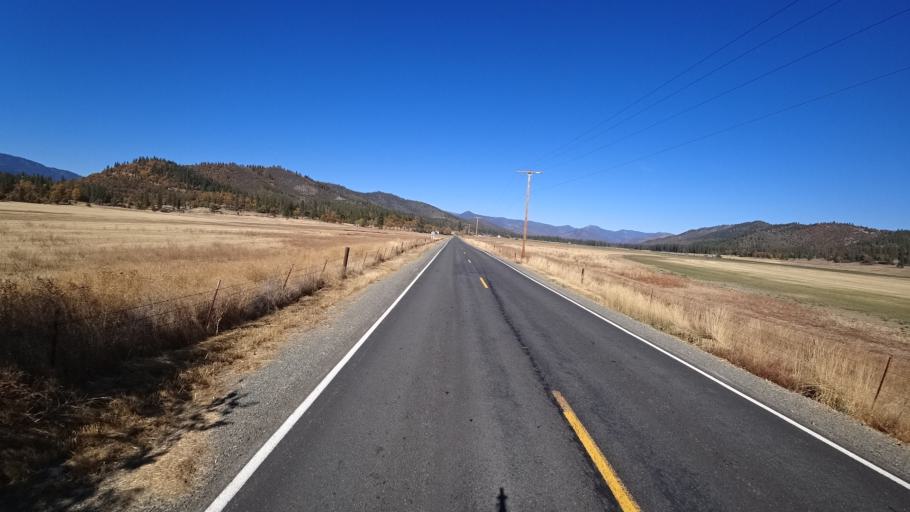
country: US
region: California
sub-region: Siskiyou County
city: Yreka
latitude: 41.5594
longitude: -122.9234
